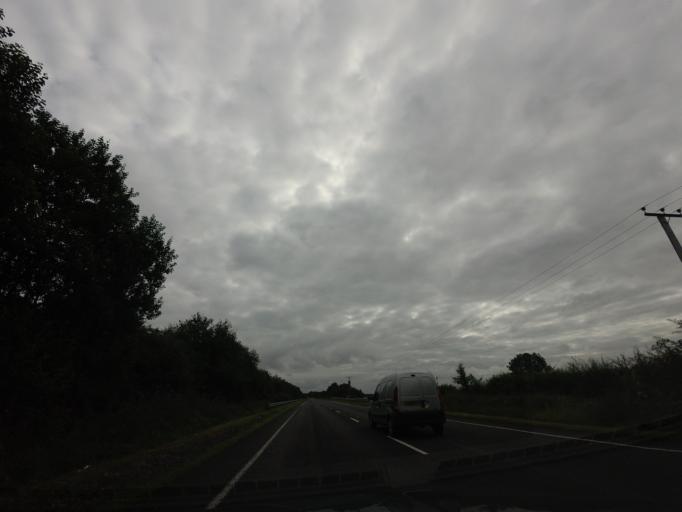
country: GB
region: Scotland
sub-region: Dumfries and Galloway
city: Gretna
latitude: 54.9921
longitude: -3.1488
